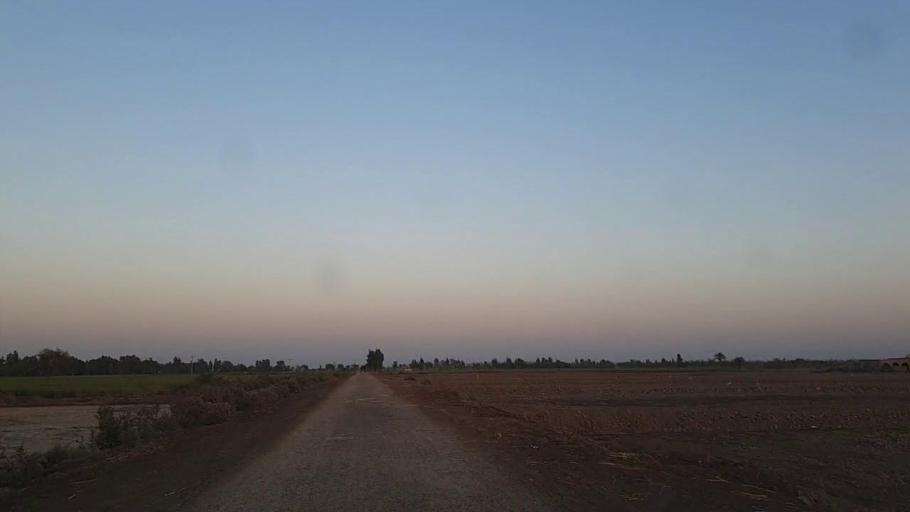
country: PK
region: Sindh
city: Samaro
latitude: 25.3107
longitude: 69.3905
